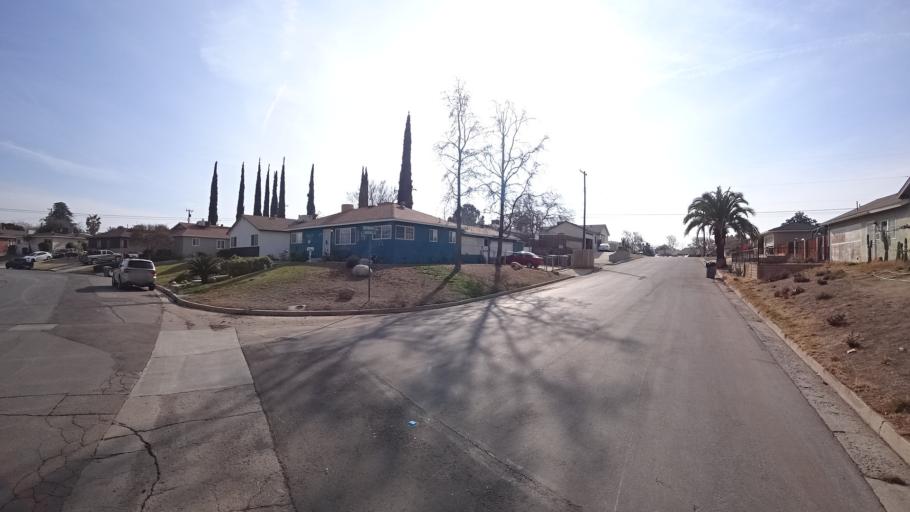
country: US
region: California
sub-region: Kern County
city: Oildale
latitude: 35.4025
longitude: -118.9786
